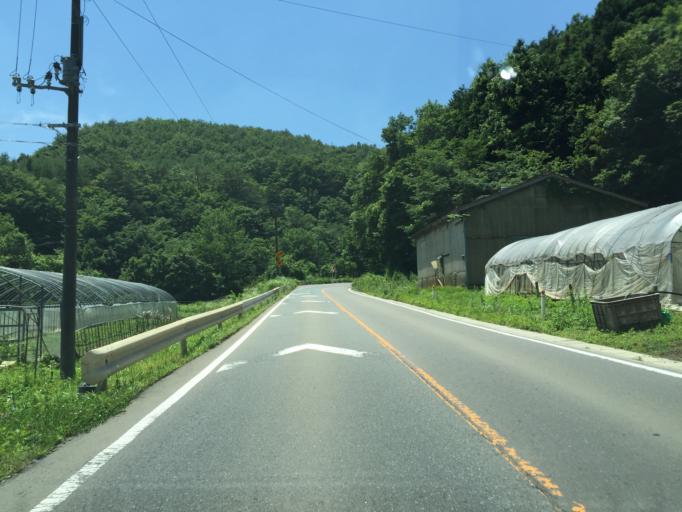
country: JP
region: Miyagi
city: Marumori
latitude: 37.7720
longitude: 140.7708
